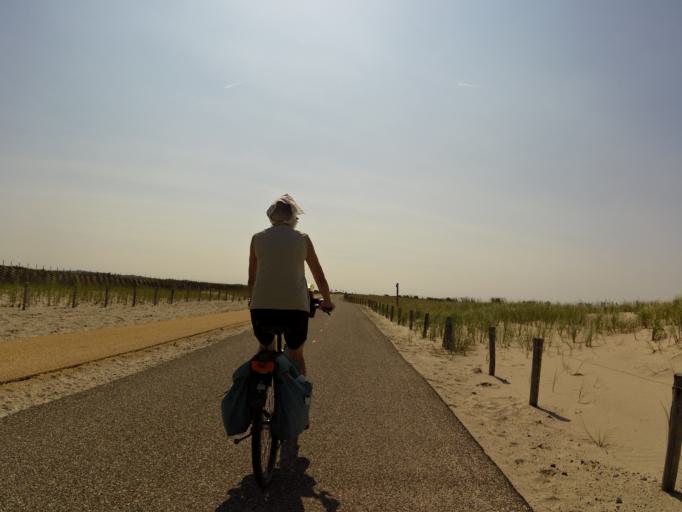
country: NL
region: North Holland
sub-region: Gemeente Schagen
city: Harenkarspel
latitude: 52.7590
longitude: 4.6502
